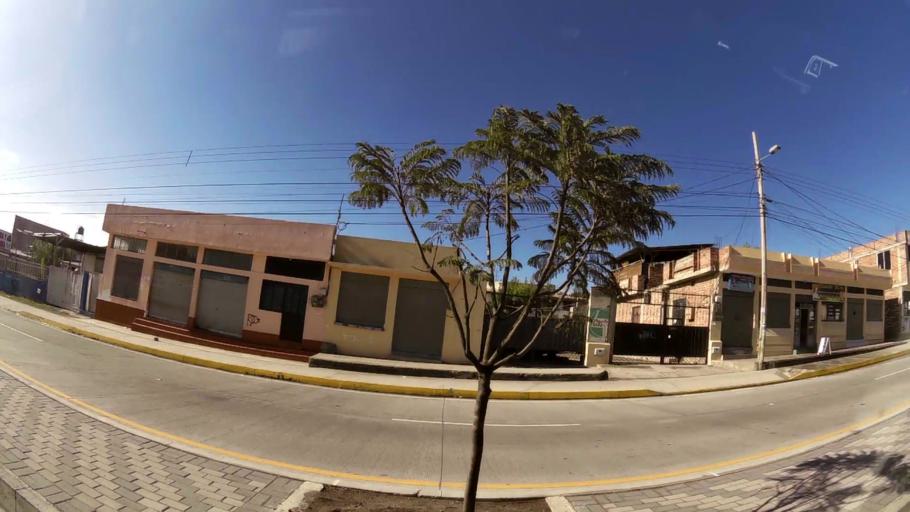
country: EC
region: Chimborazo
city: Riobamba
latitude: -1.6588
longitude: -78.6859
